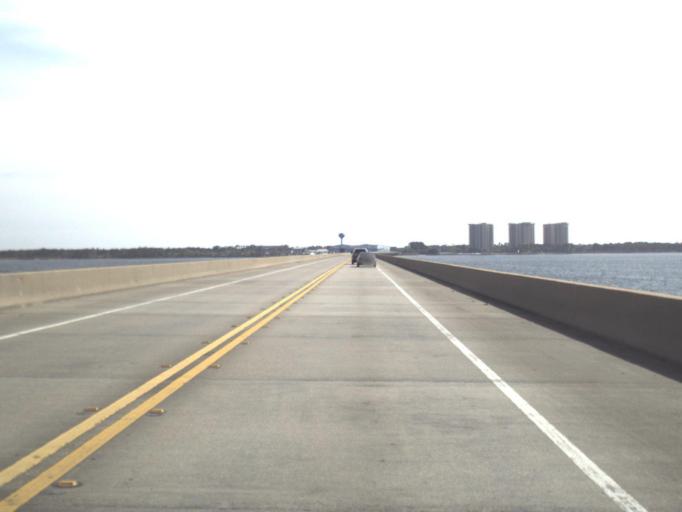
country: US
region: Florida
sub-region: Walton County
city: Miramar Beach
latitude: 30.4181
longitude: -86.4216
